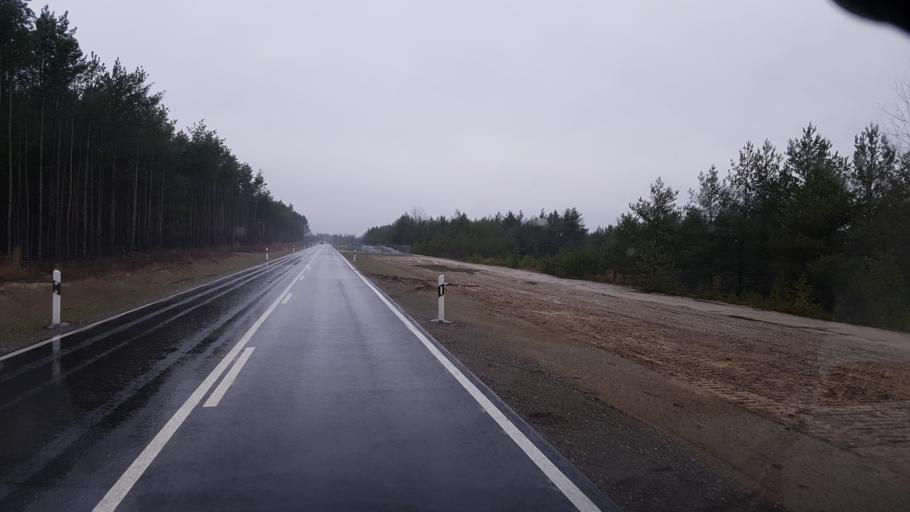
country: DE
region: Brandenburg
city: Lauchhammer
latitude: 51.5229
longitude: 13.7911
